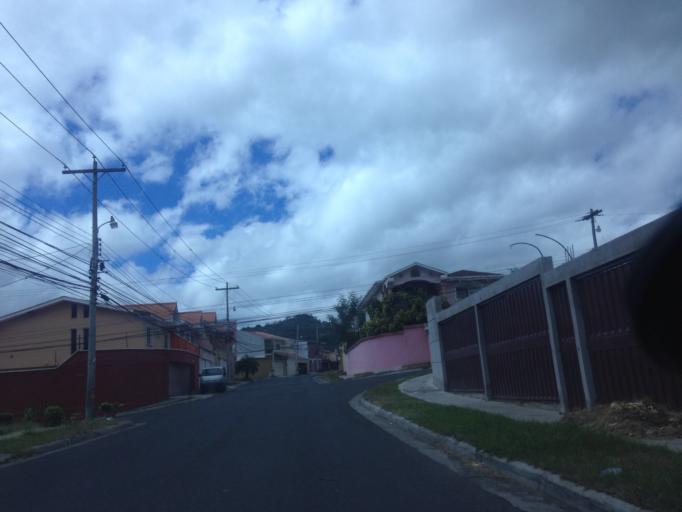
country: HN
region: Francisco Morazan
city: Yaguacire
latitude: 14.0435
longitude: -87.2320
